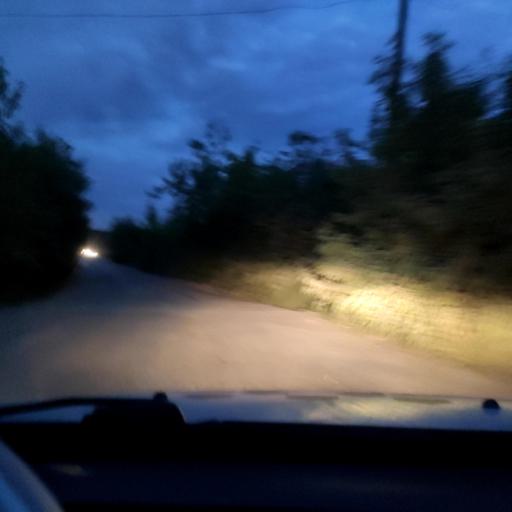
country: RU
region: Perm
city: Kondratovo
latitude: 58.0298
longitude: 56.0625
